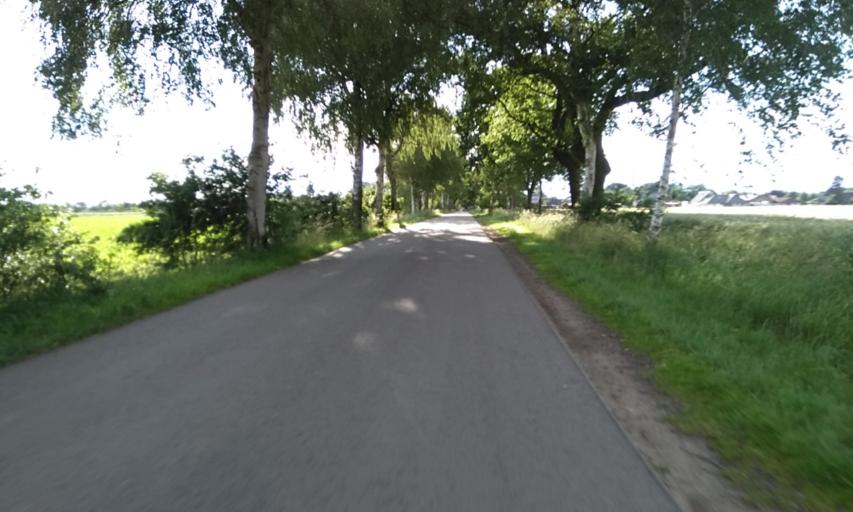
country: DE
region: Lower Saxony
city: Ahlerstedt
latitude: 53.3623
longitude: 9.4335
